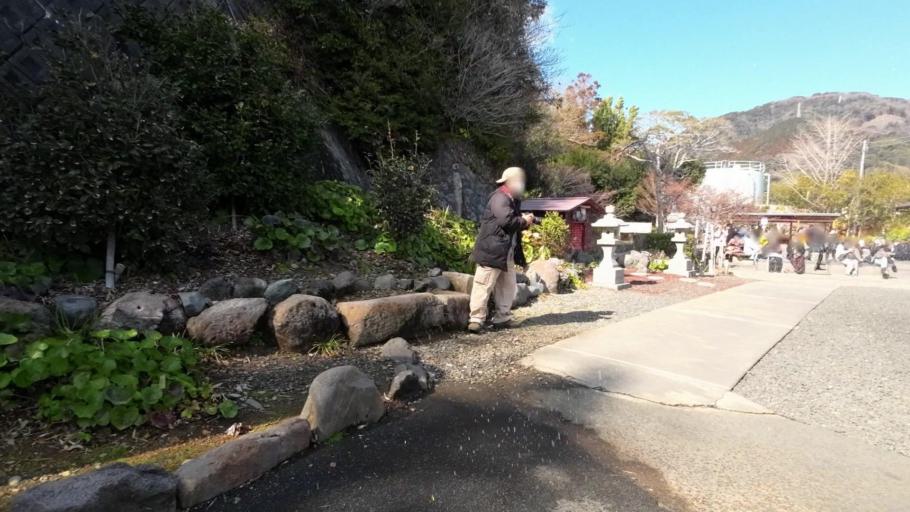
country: JP
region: Shizuoka
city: Shimoda
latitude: 34.7570
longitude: 138.9824
